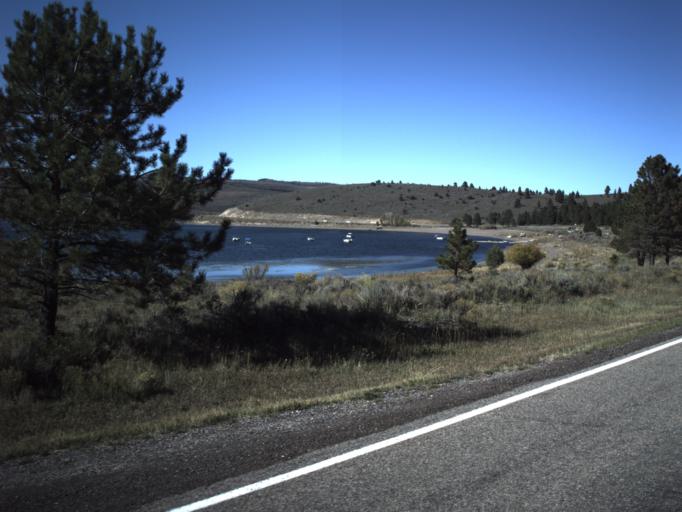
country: US
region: Utah
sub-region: Garfield County
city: Panguitch
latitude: 37.7096
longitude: -112.6251
